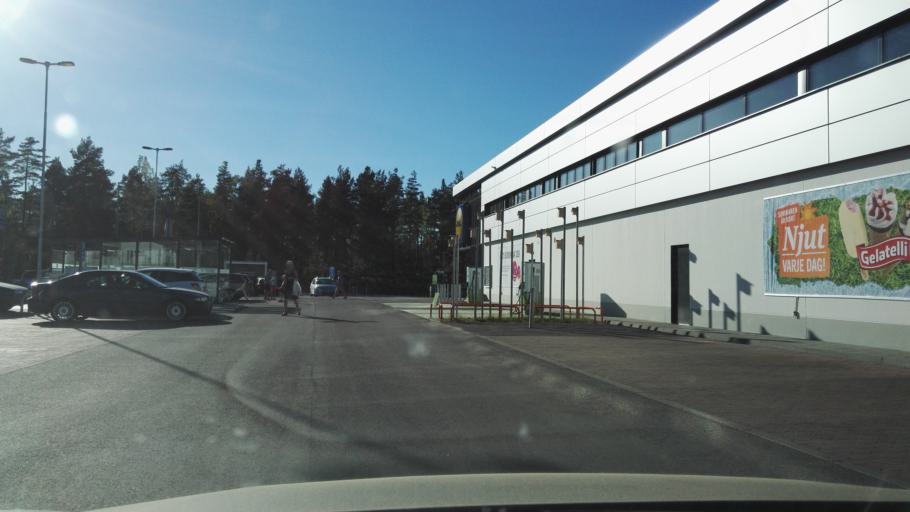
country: SE
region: Kronoberg
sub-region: Vaxjo Kommun
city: Vaexjoe
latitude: 56.9001
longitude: 14.8257
